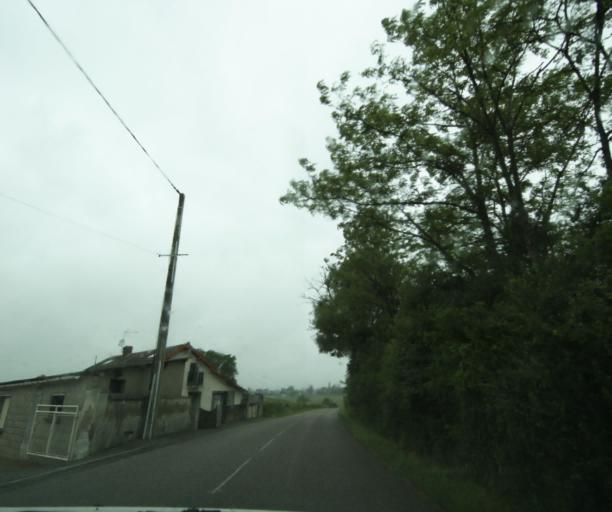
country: FR
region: Bourgogne
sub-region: Departement de Saone-et-Loire
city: Palinges
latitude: 46.5541
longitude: 4.1966
